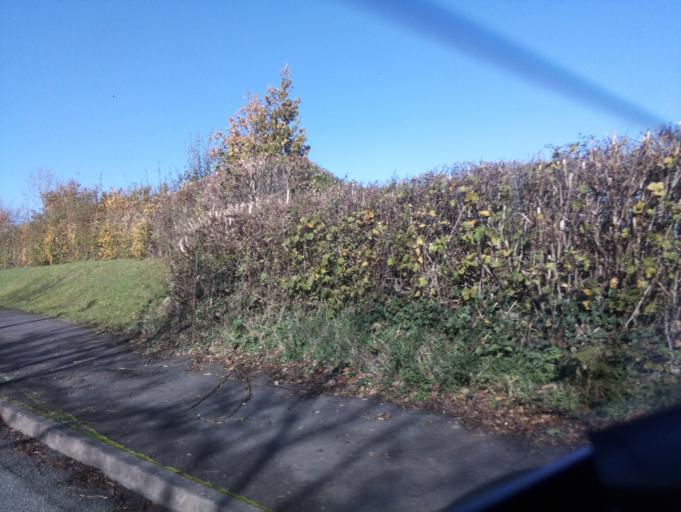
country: GB
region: England
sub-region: Somerset
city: Yeovil
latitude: 50.9599
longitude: -2.6597
